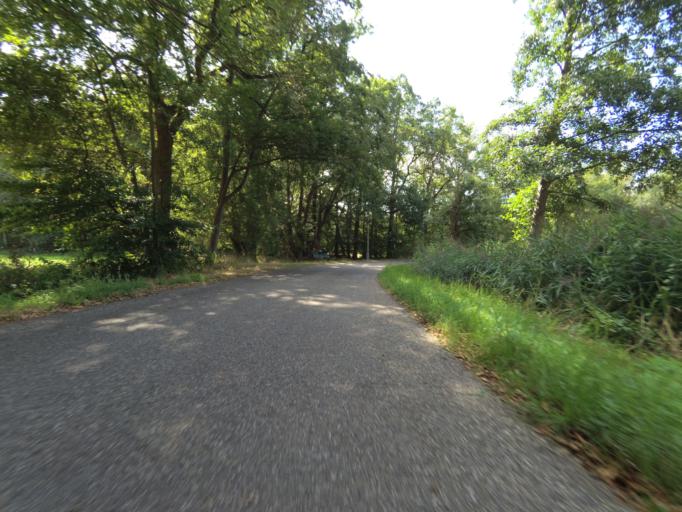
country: NL
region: Overijssel
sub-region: Gemeente Hengelo
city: Hengelo
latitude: 52.2526
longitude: 6.8317
